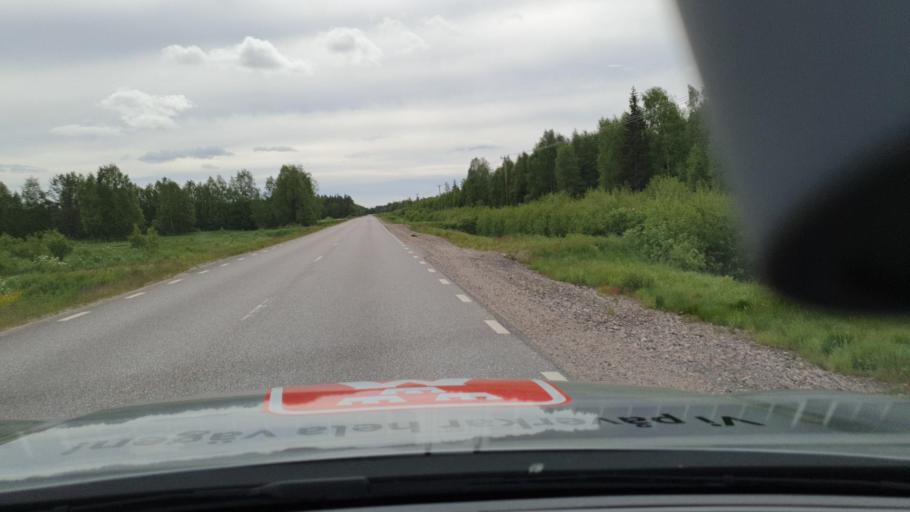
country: SE
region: Norrbotten
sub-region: Kalix Kommun
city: Kalix
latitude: 65.8867
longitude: 23.4728
